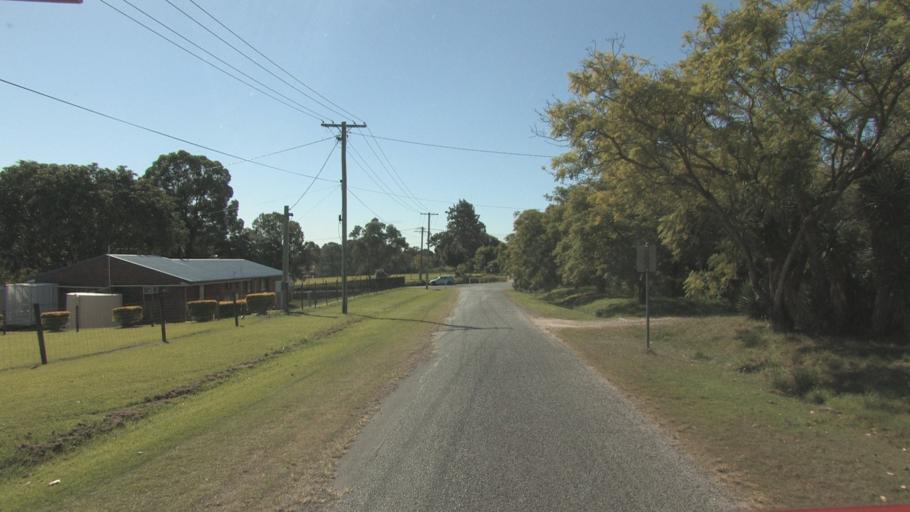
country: AU
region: Queensland
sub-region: Logan
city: Waterford West
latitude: -27.7155
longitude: 153.1267
